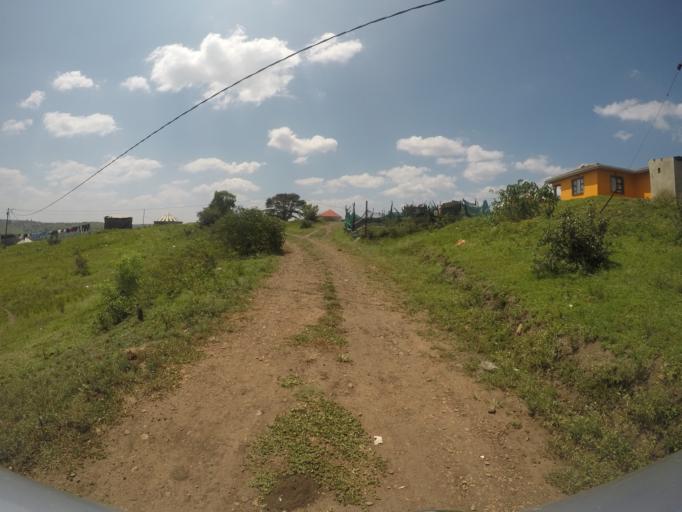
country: ZA
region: KwaZulu-Natal
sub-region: uThungulu District Municipality
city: Empangeni
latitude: -28.5968
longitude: 31.7376
